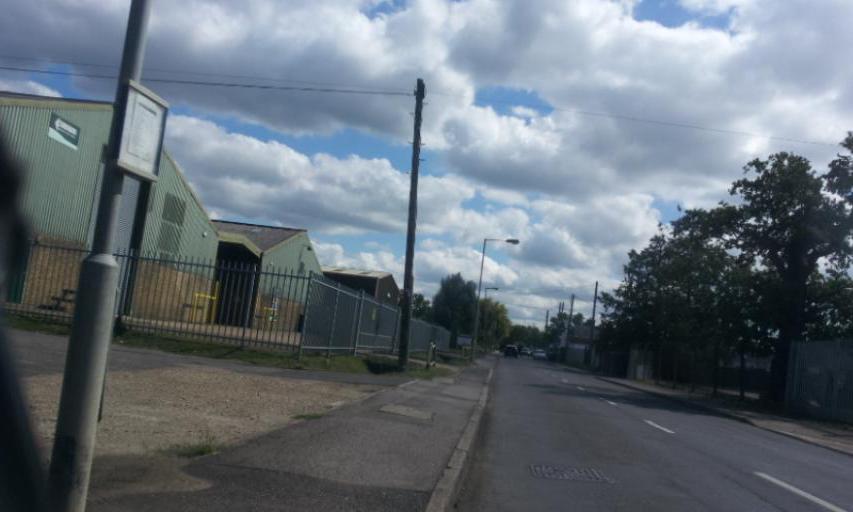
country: GB
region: England
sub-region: Kent
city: Marden
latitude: 51.1783
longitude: 0.4889
